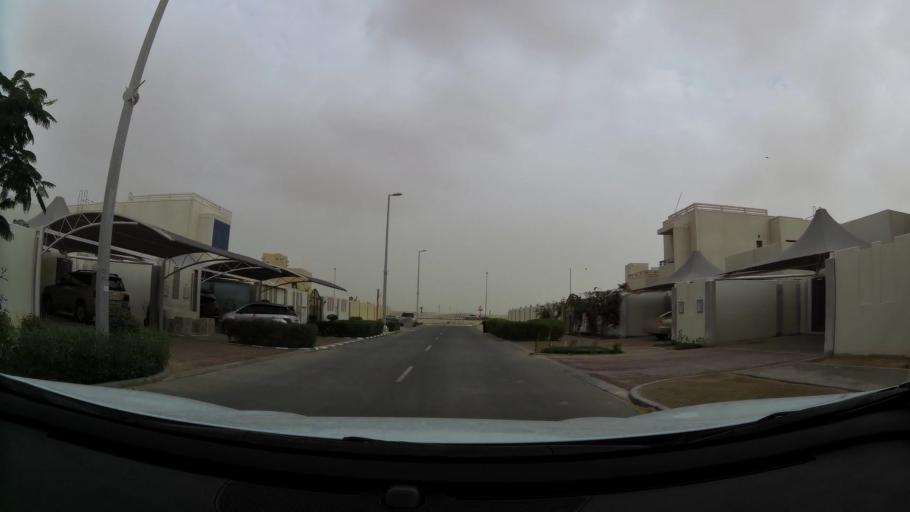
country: AE
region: Abu Dhabi
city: Abu Dhabi
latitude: 24.4599
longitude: 54.7144
